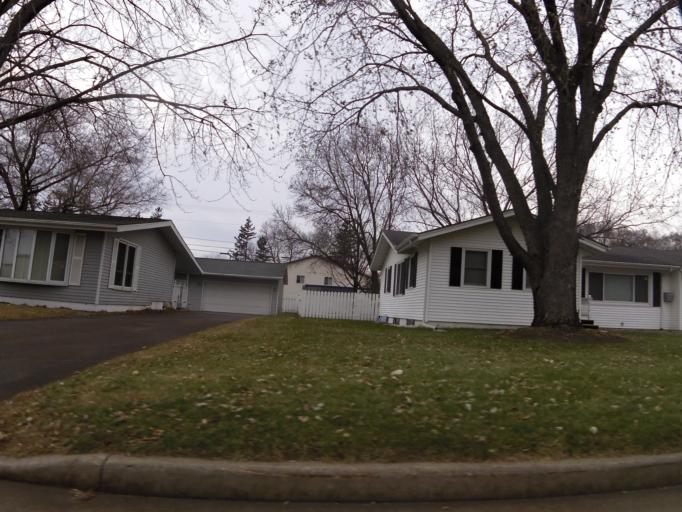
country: US
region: Wisconsin
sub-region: Pierce County
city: River Falls
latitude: 44.8528
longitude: -92.6091
